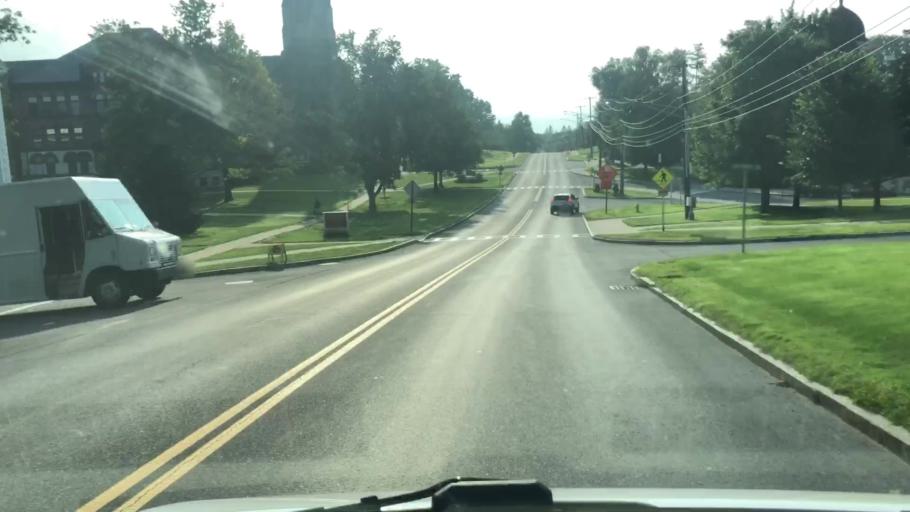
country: US
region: Massachusetts
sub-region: Berkshire County
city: Williamstown
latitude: 42.7126
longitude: -73.2047
